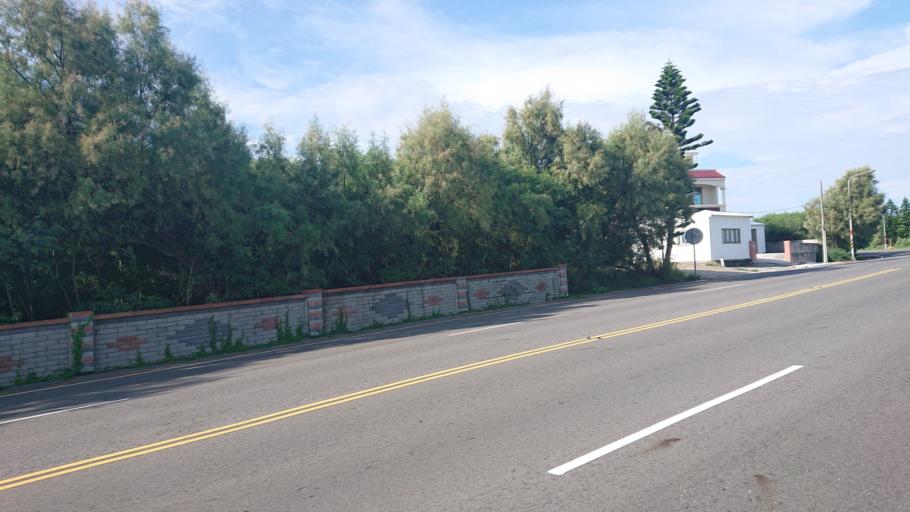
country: TW
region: Taiwan
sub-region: Penghu
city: Ma-kung
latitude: 23.5206
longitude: 119.5814
